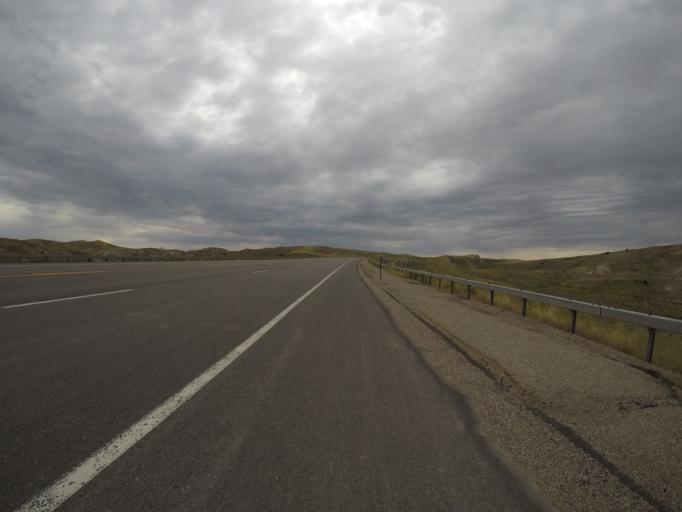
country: US
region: Wyoming
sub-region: Lincoln County
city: Kemmerer
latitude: 41.8089
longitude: -110.6131
